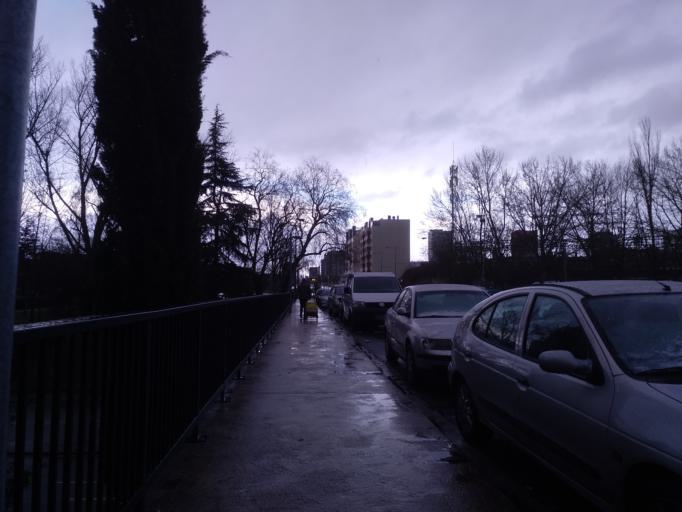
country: ES
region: Basque Country
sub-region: Provincia de Alava
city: Gasteiz / Vitoria
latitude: 42.8482
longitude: -2.6580
